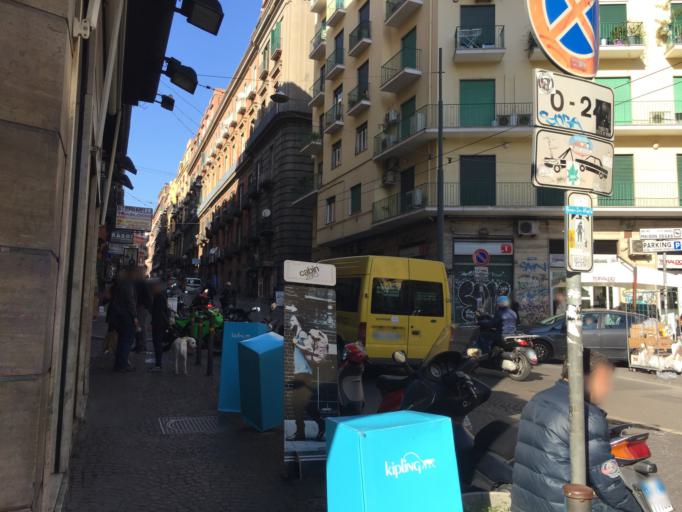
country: IT
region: Campania
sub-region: Provincia di Napoli
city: Napoli
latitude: 40.8454
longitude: 14.2509
